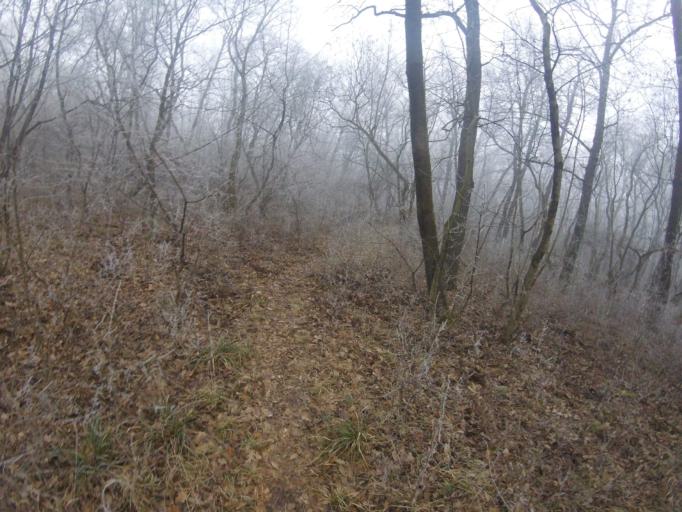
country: HU
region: Fejer
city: Zamoly
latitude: 47.3757
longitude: 18.3900
